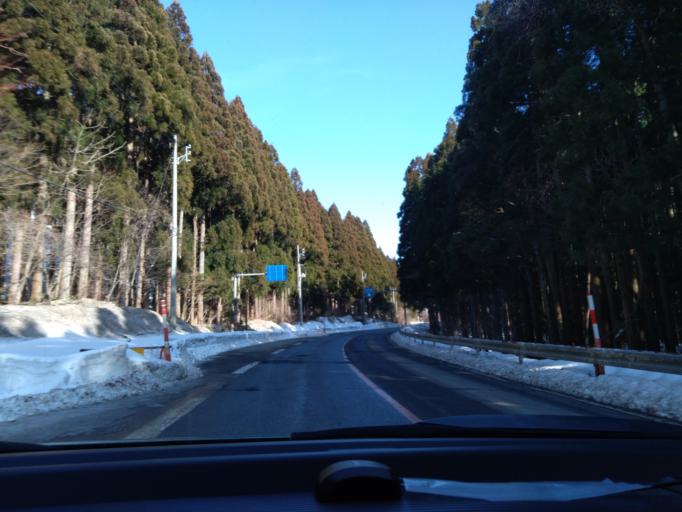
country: JP
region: Akita
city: Kakunodatemachi
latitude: 39.7043
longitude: 140.7471
